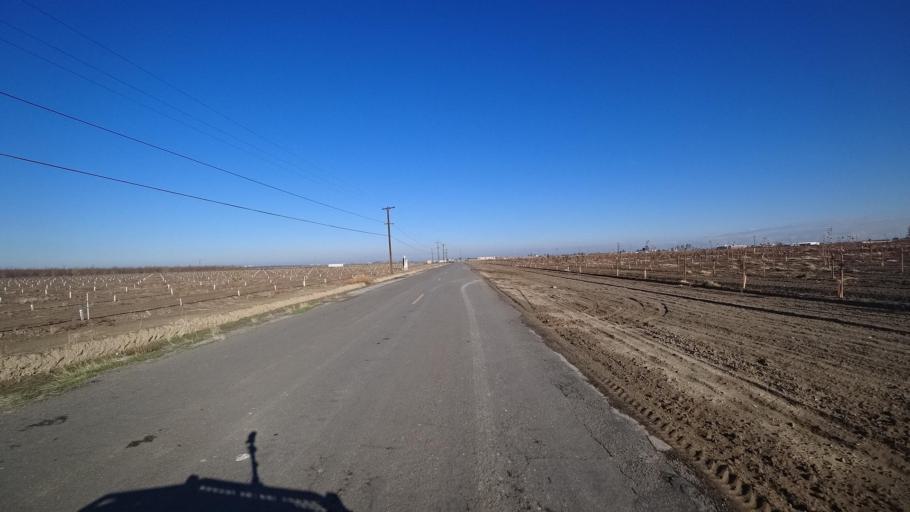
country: US
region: California
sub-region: Kern County
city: Delano
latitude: 35.7586
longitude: -119.3119
